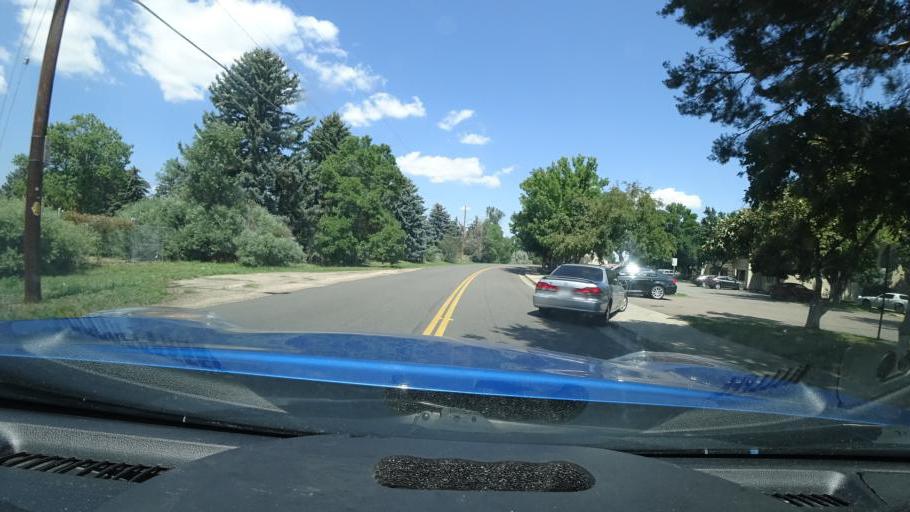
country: US
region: Colorado
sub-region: Arapahoe County
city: Glendale
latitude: 39.7069
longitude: -104.8919
